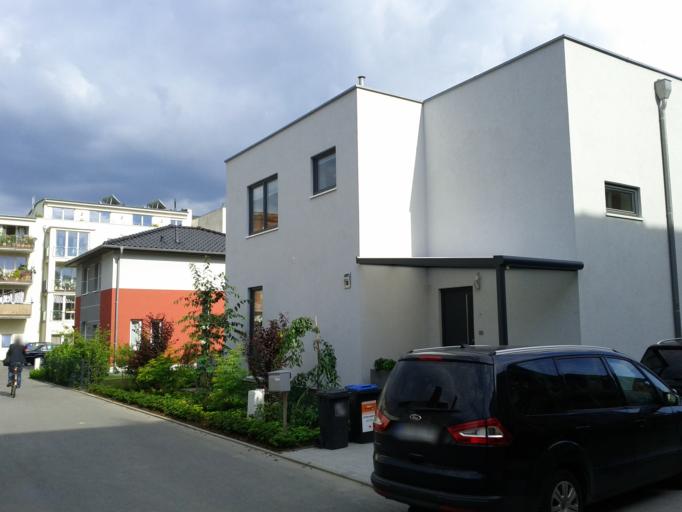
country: DE
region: Berlin
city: Friedrichshagen
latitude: 52.4525
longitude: 13.6196
